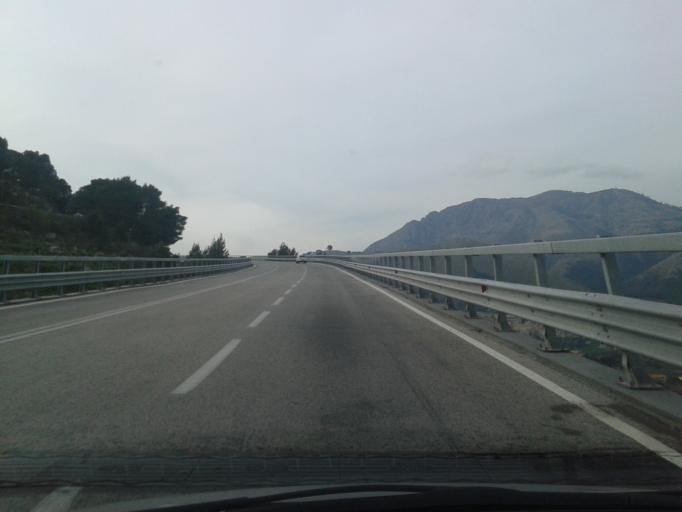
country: IT
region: Sicily
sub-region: Palermo
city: Giacalone
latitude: 38.0372
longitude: 13.2409
